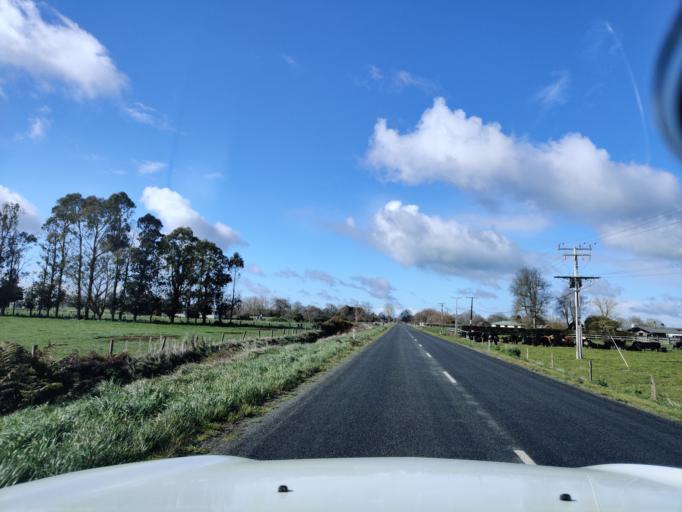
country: NZ
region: Waikato
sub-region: Waikato District
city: Ngaruawahia
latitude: -37.6060
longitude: 175.3053
